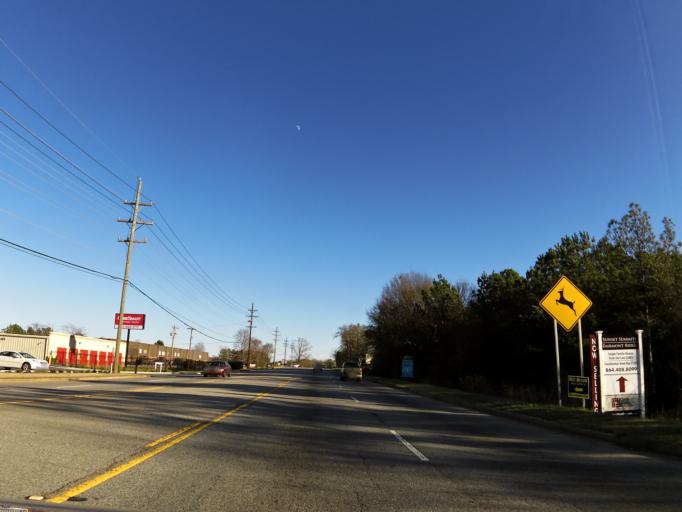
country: US
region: South Carolina
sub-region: Spartanburg County
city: Wellford
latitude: 34.8947
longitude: -82.0855
